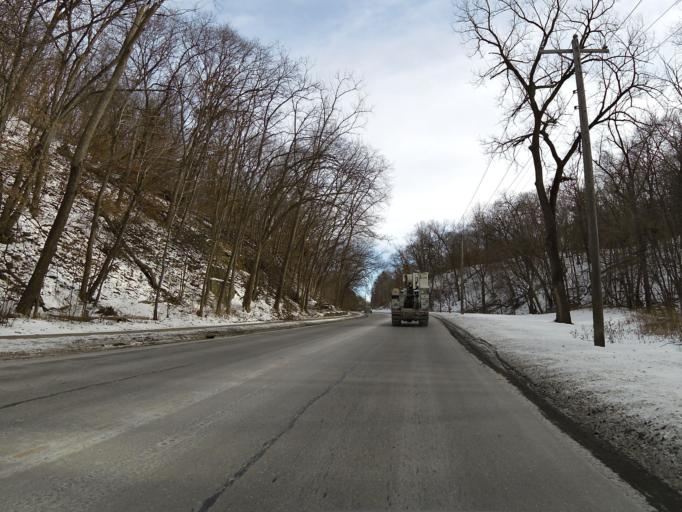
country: US
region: Wisconsin
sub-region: Saint Croix County
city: Hudson
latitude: 44.9697
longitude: -92.7542
